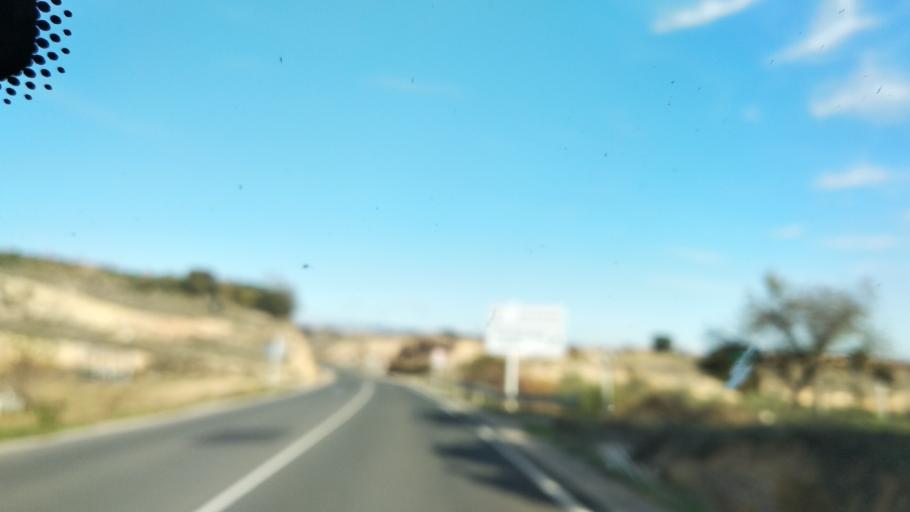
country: ES
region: Catalonia
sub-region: Provincia de Lleida
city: Termens
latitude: 41.7270
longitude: 0.7328
